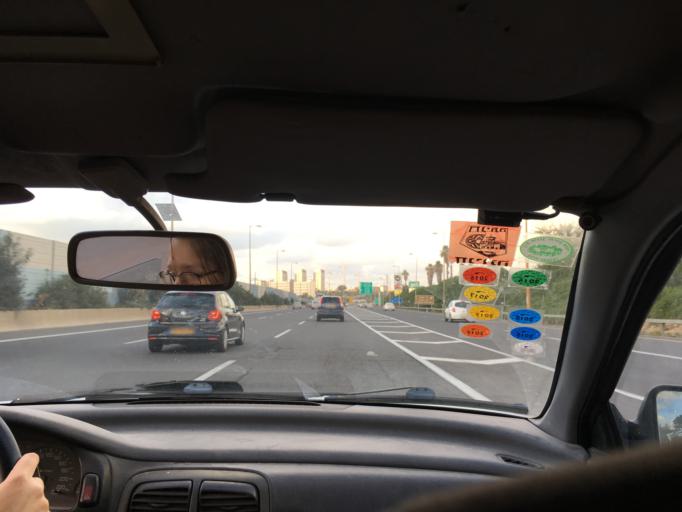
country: IL
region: Tel Aviv
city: Ramat Gan
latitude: 32.0954
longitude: 34.8021
